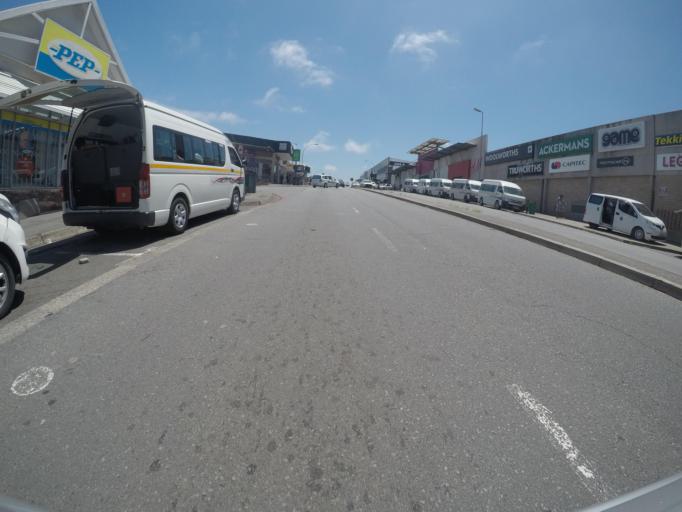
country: ZA
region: Eastern Cape
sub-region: Buffalo City Metropolitan Municipality
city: East London
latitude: -32.9845
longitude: 27.9042
